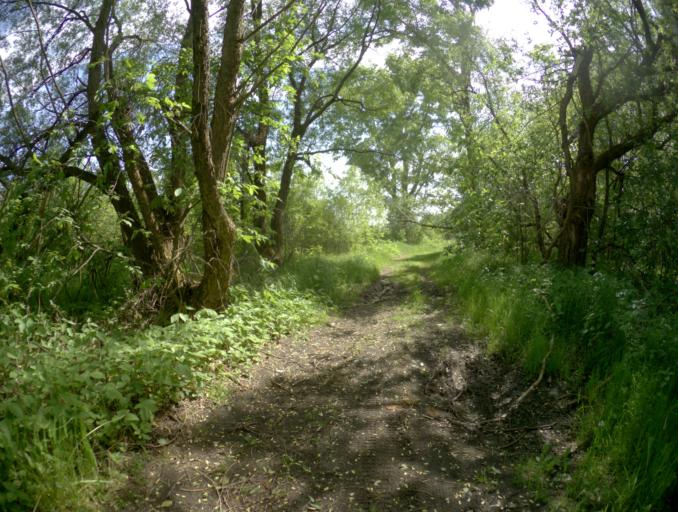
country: RU
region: Vladimir
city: Ivanishchi
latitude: 55.6666
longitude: 40.3881
